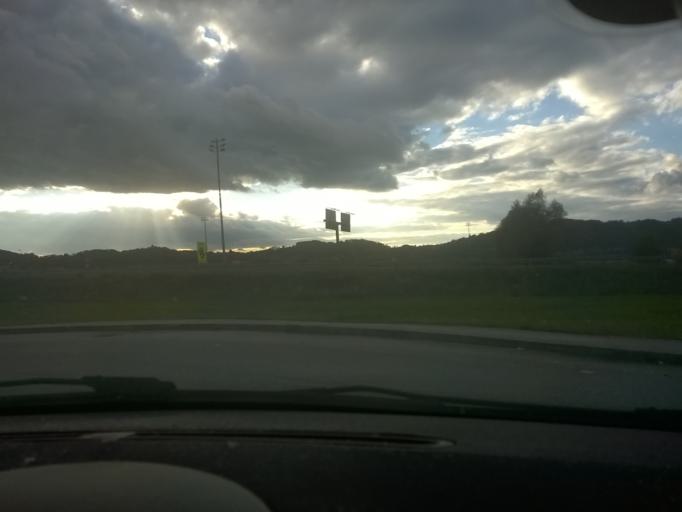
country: HR
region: Krapinsko-Zagorska
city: Zabok
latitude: 46.0912
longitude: 15.9102
